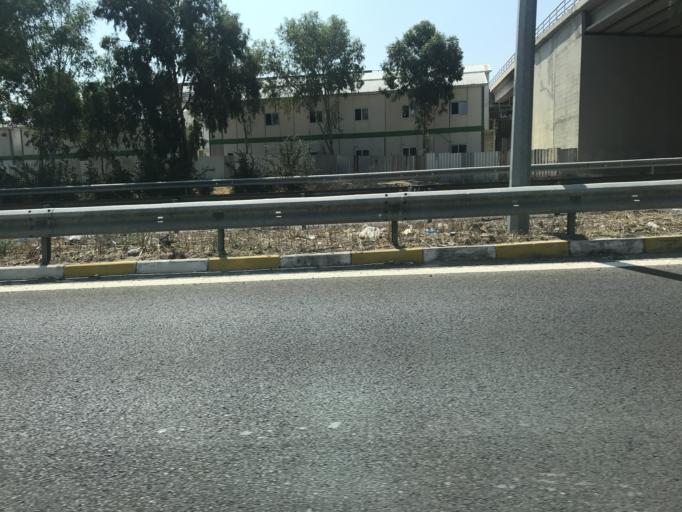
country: TR
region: Izmir
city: Karsiyaka
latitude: 38.3981
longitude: 27.0626
